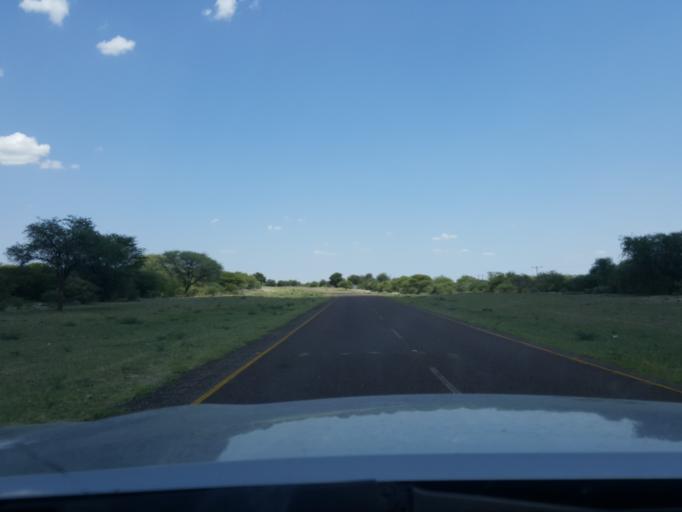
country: BW
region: North West
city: Maun
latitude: -20.2669
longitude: 23.1102
